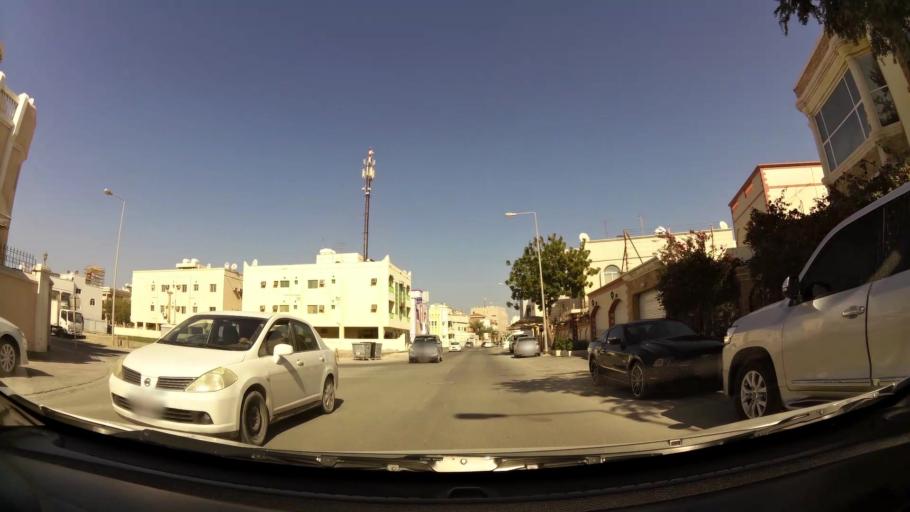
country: BH
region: Manama
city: Manama
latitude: 26.2092
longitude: 50.5722
